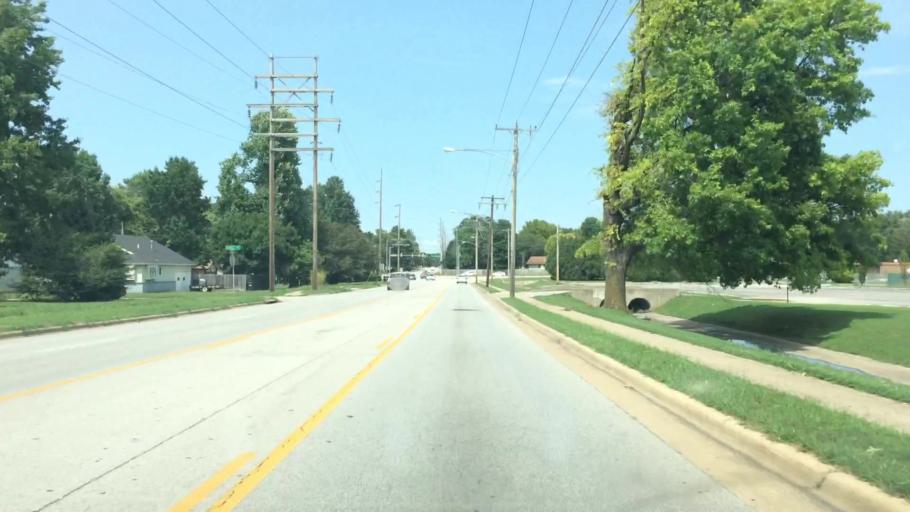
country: US
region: Missouri
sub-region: Greene County
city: Springfield
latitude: 37.1650
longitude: -93.2716
